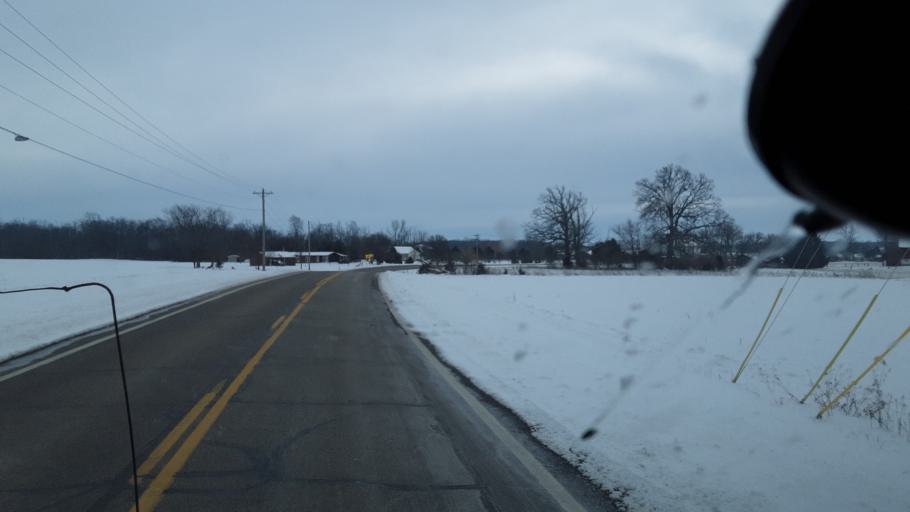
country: US
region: Ohio
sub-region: Champaign County
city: Mechanicsburg
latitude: 40.0519
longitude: -83.5315
